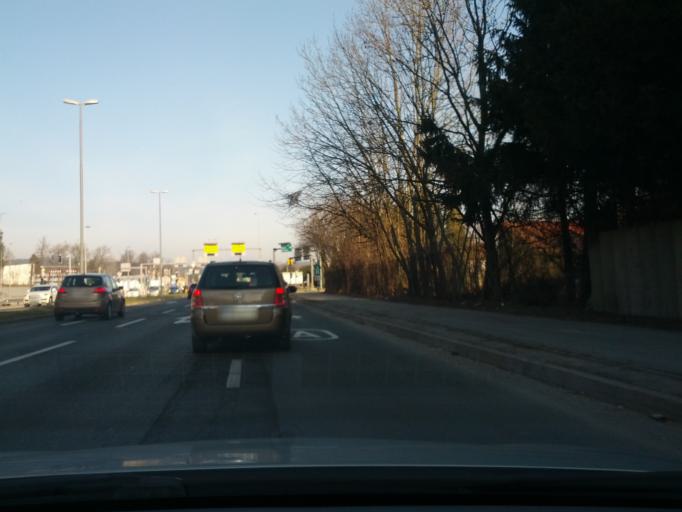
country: SI
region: Medvode
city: Zgornje Pirnice
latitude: 46.0970
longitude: 14.4647
